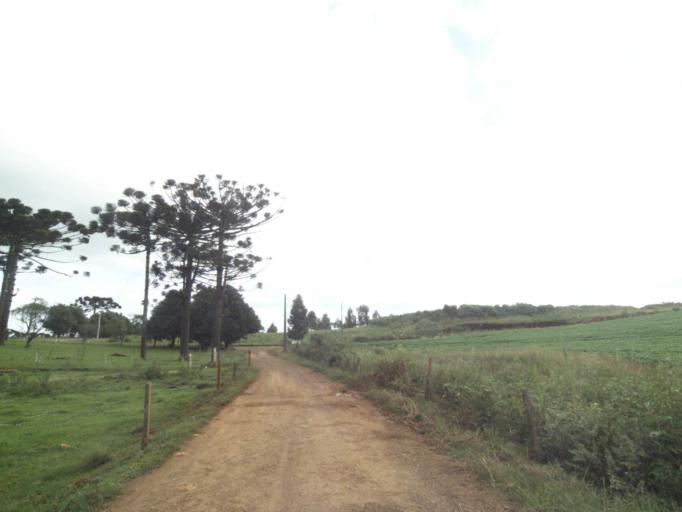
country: BR
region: Rio Grande do Sul
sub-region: Lagoa Vermelha
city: Lagoa Vermelha
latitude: -28.2029
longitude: -51.5094
